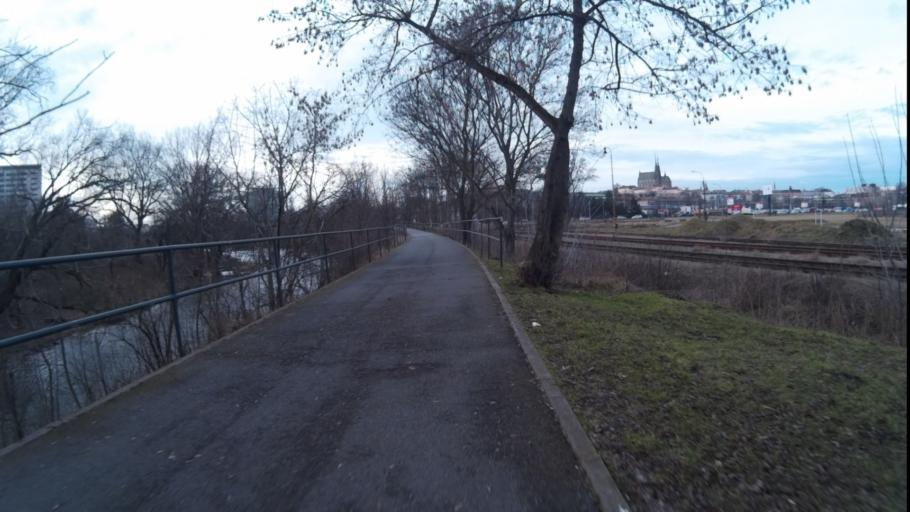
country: CZ
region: South Moravian
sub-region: Mesto Brno
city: Brno
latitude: 49.1826
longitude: 16.6098
